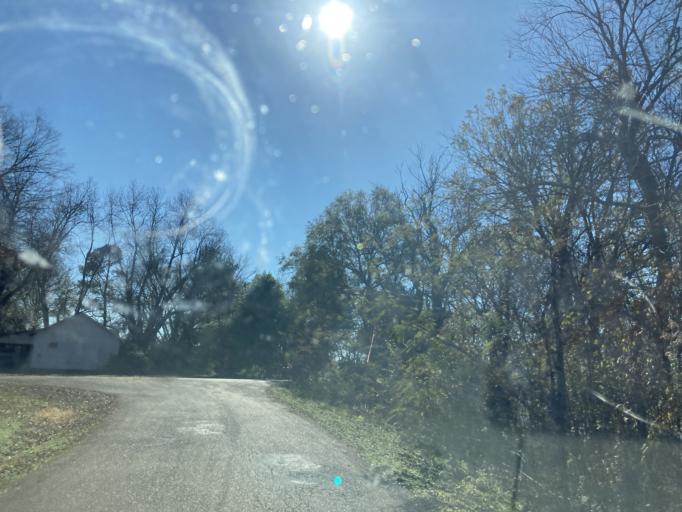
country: US
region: Mississippi
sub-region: Yazoo County
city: Yazoo City
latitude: 32.9236
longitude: -90.4940
